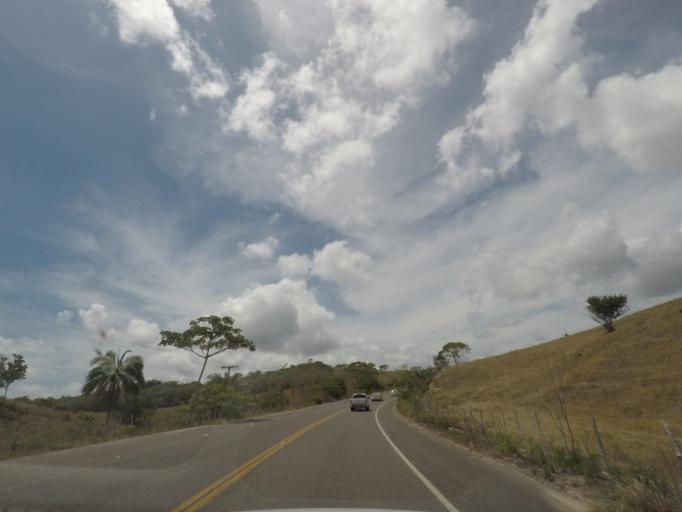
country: BR
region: Sergipe
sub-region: Indiaroba
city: Indiaroba
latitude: -11.4993
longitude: -37.4919
